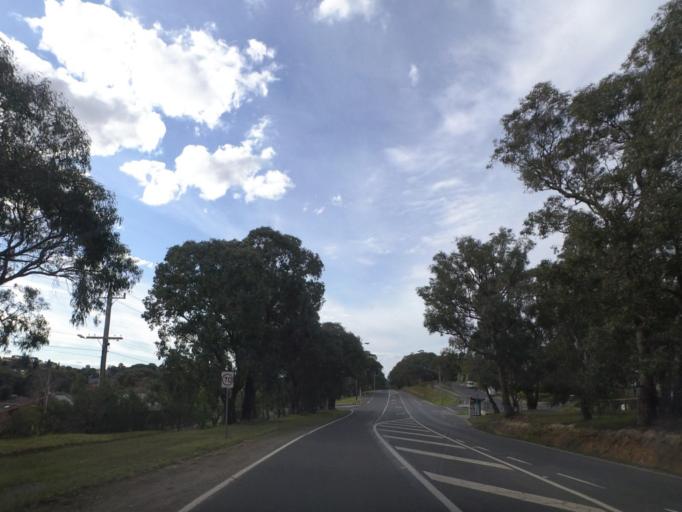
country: AU
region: Victoria
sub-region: Manningham
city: Donvale
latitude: -37.7568
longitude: 145.1734
